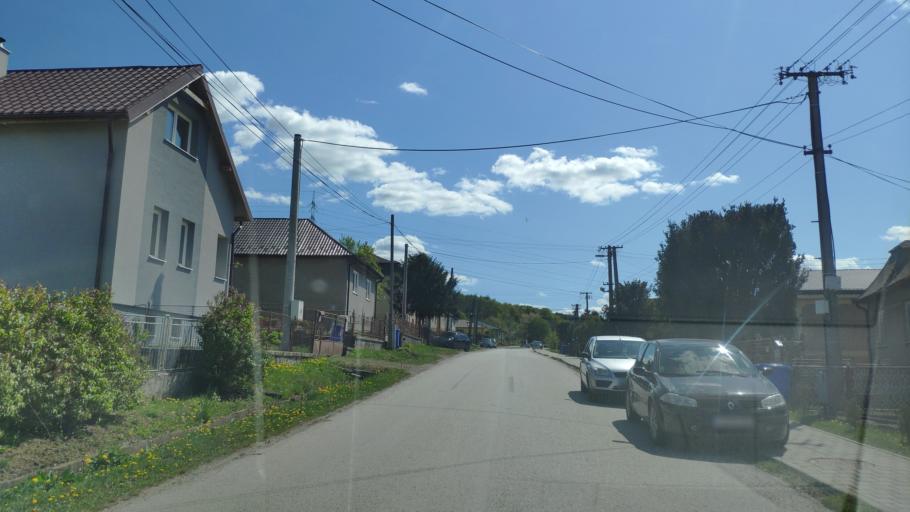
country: SK
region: Kosicky
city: Kosice
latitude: 48.6780
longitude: 21.4309
